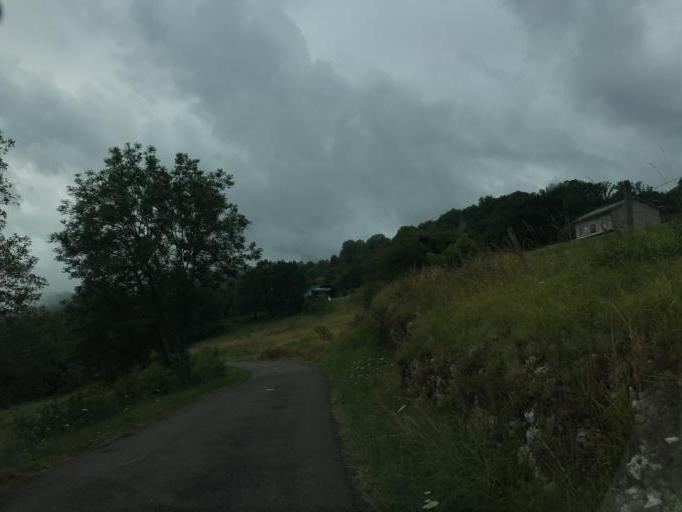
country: FR
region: Franche-Comte
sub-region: Departement du Jura
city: Lavans-les-Saint-Claude
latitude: 46.3286
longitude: 5.7553
